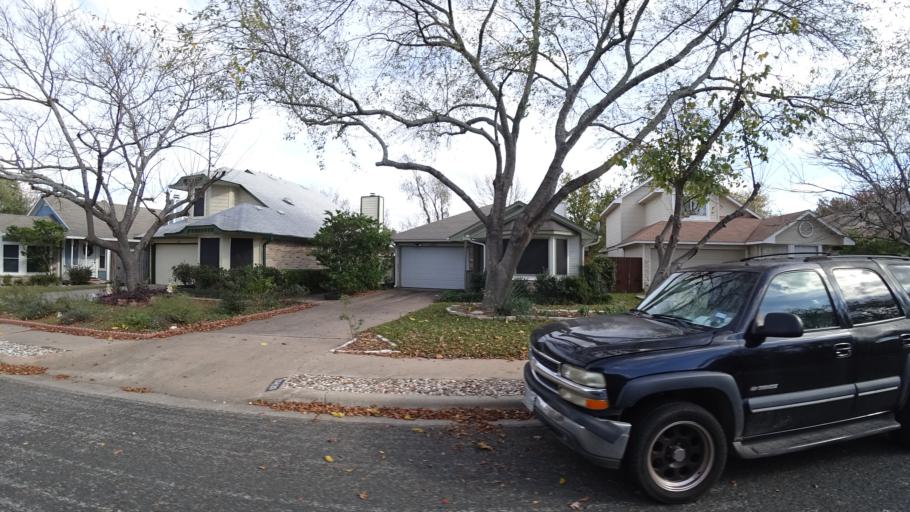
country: US
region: Texas
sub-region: Williamson County
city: Brushy Creek
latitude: 30.5088
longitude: -97.7379
